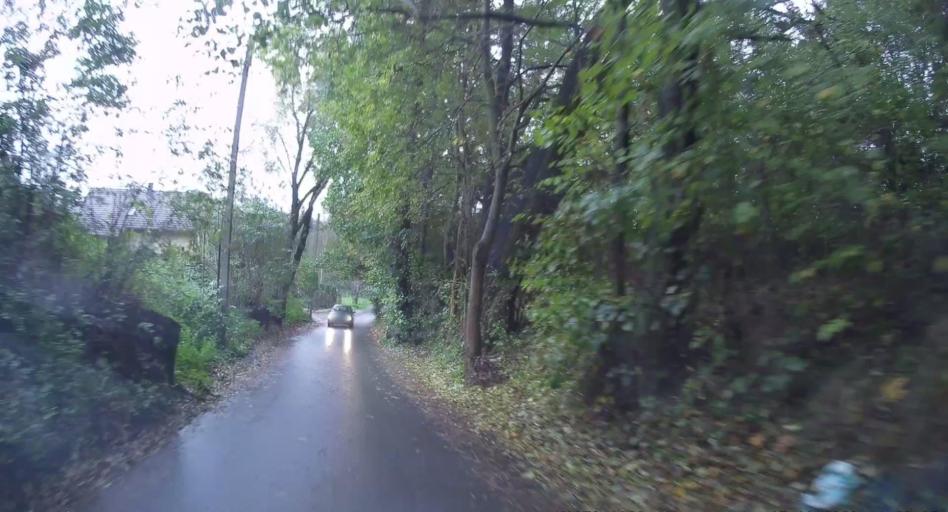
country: PL
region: Lesser Poland Voivodeship
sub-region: Powiat krakowski
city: Ochojno
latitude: 49.9904
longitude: 19.9891
